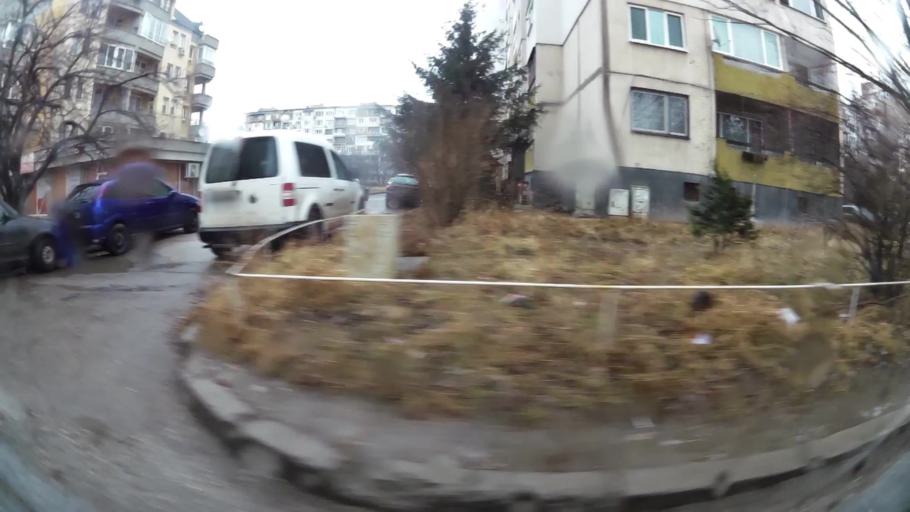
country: BG
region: Sofia-Capital
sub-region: Stolichna Obshtina
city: Sofia
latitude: 42.6529
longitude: 23.3696
